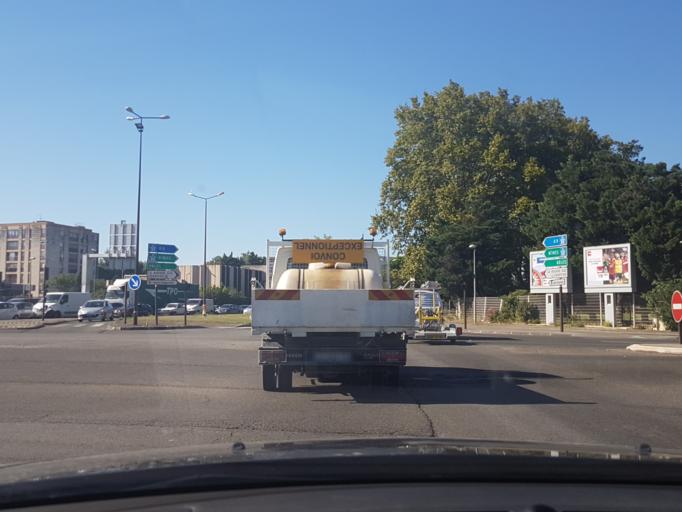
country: FR
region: Provence-Alpes-Cote d'Azur
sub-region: Departement du Vaucluse
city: Avignon
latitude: 43.9344
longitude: 4.8316
